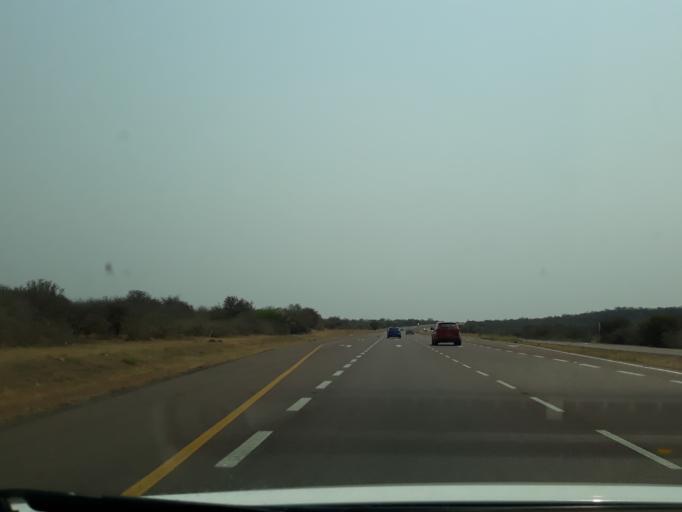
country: BW
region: Kgatleng
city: Bokaa
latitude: -24.4267
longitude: 26.0472
